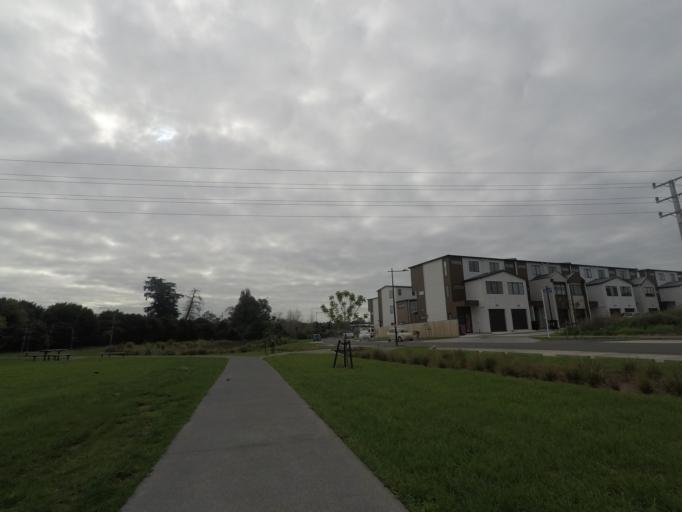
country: NZ
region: Auckland
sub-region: Auckland
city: Waitakere
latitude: -36.8981
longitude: 174.6301
